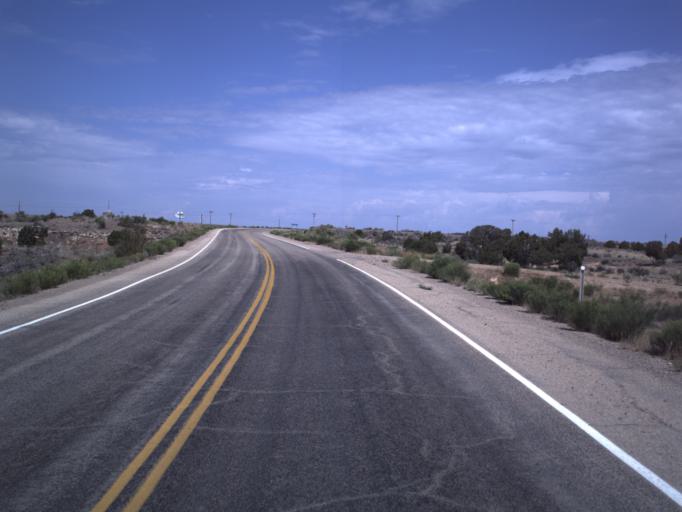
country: US
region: Utah
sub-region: Uintah County
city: Naples
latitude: 40.1816
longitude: -109.3253
